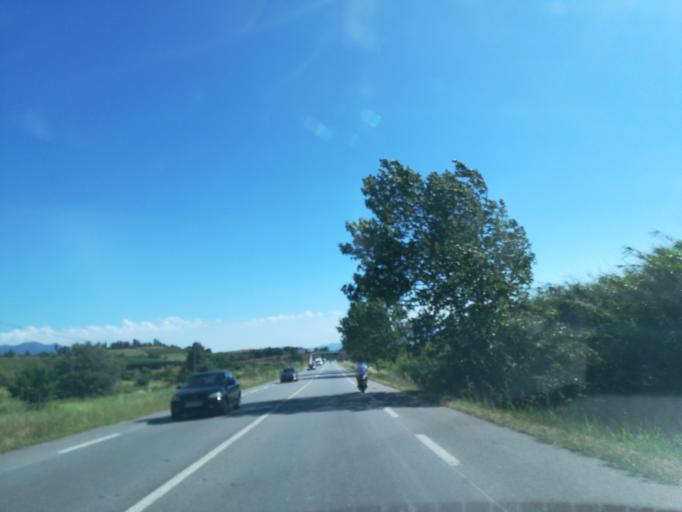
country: FR
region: Languedoc-Roussillon
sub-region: Departement des Pyrenees-Orientales
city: Pollestres
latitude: 42.6119
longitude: 2.8623
